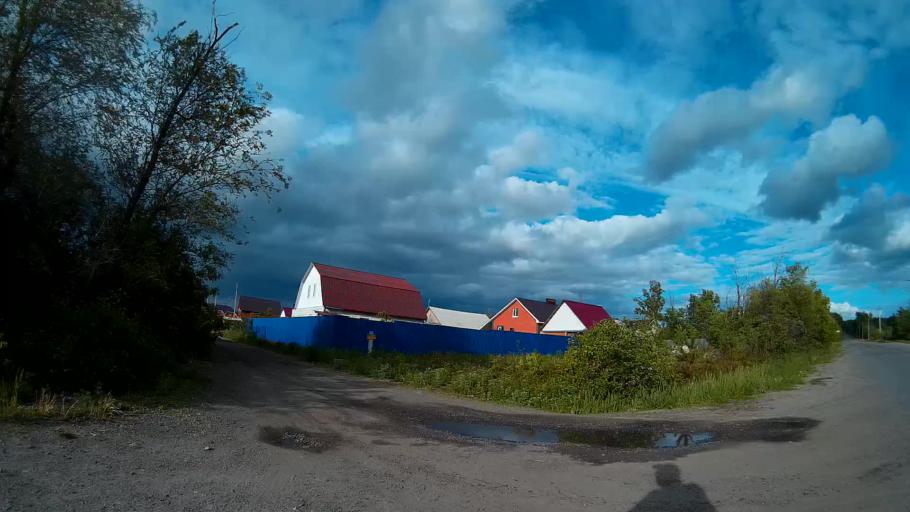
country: RU
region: Ulyanovsk
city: Novoul'yanovsk
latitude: 54.1997
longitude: 48.2725
